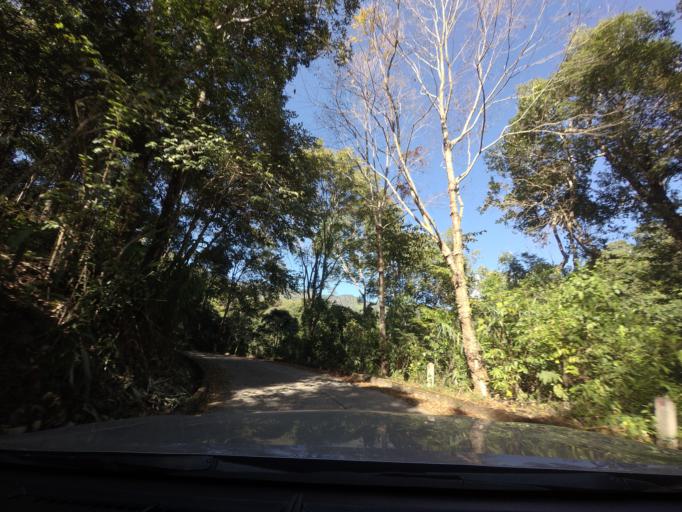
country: TH
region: Chiang Mai
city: Mae On
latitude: 18.8397
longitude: 99.3743
